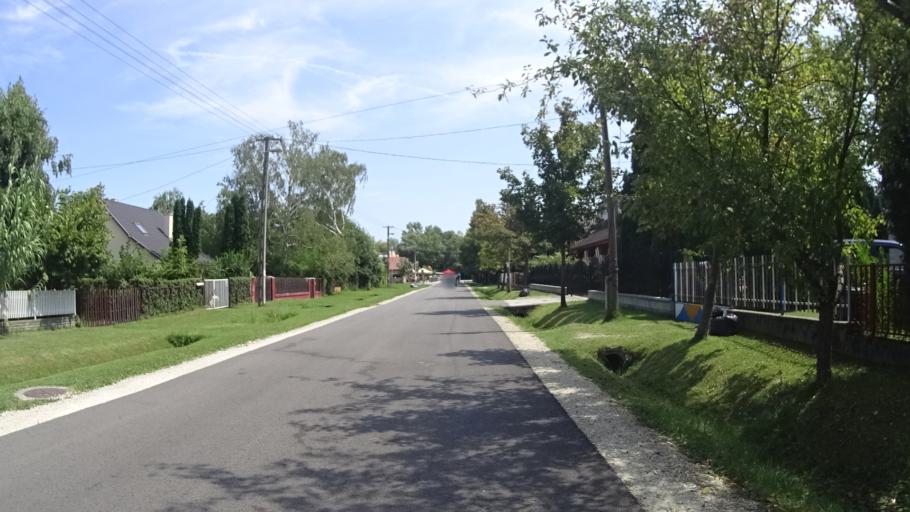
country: HU
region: Somogy
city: Balatonfenyves
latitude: 46.7055
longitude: 17.4328
